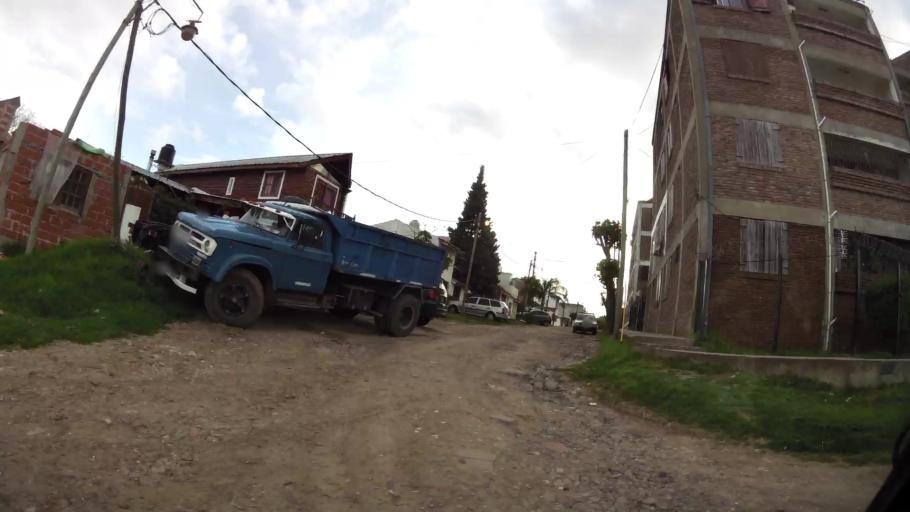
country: AR
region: Buenos Aires
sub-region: Partido de Quilmes
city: Quilmes
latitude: -34.7277
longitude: -58.2339
